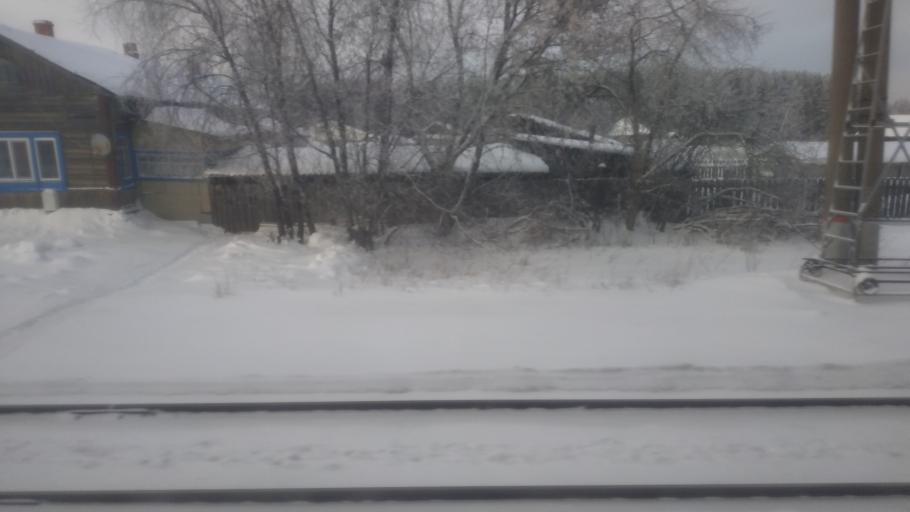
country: RU
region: Udmurtiya
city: Kizner
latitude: 56.3875
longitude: 51.7179
